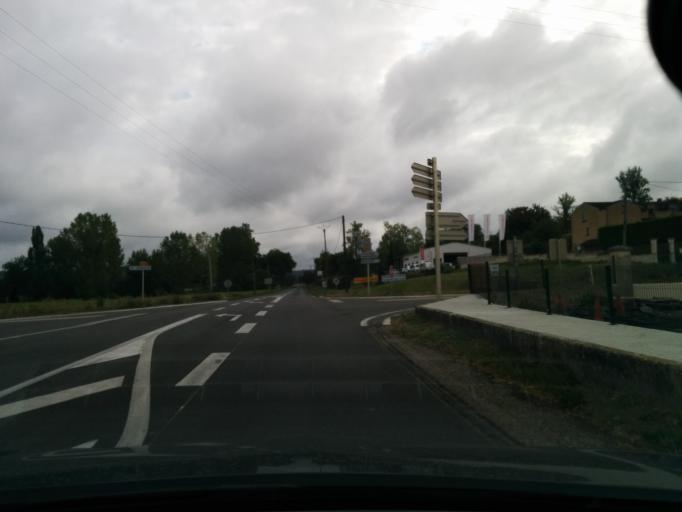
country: FR
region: Midi-Pyrenees
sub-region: Departement du Lot
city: Montcuq
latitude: 44.3435
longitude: 1.2087
